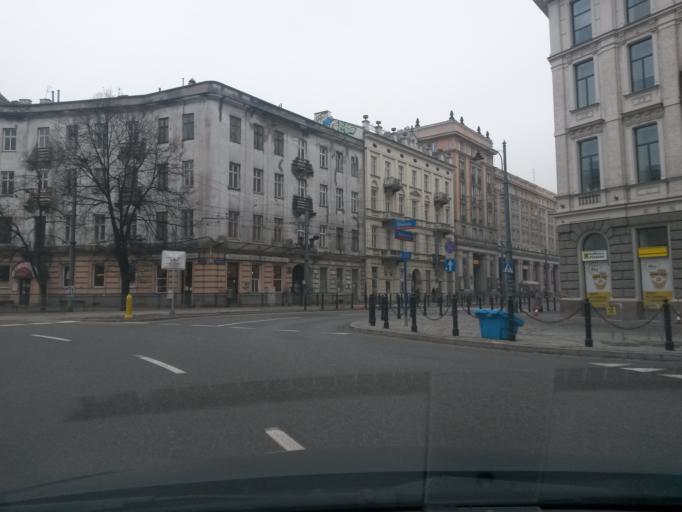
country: PL
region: Masovian Voivodeship
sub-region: Warszawa
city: Srodmiescie
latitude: 52.2201
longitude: 21.0181
